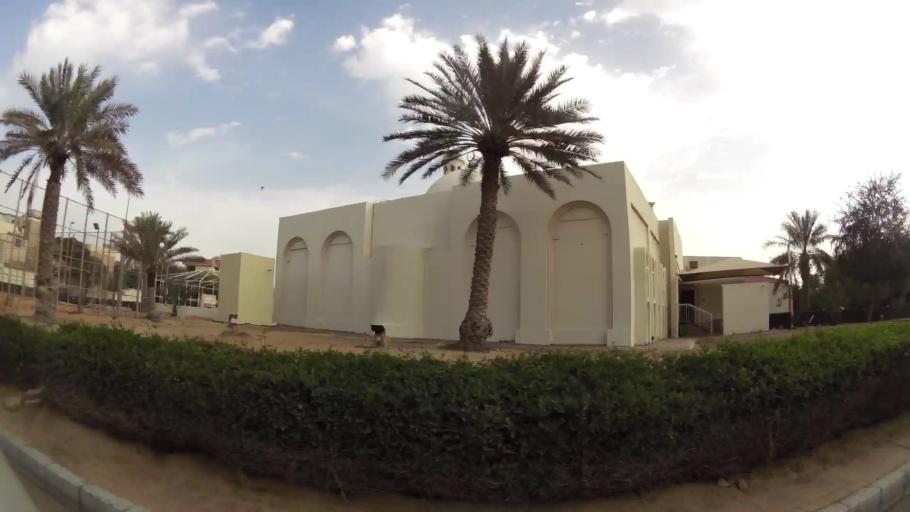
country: AE
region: Abu Dhabi
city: Abu Dhabi
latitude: 24.4330
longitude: 54.3729
